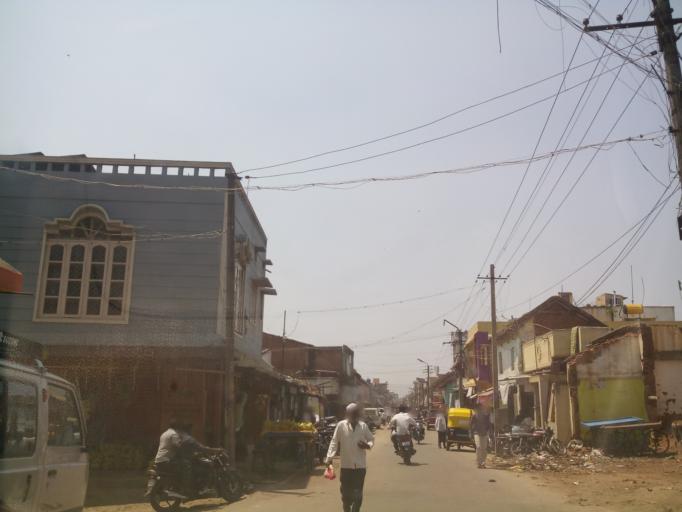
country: IN
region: Karnataka
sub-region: Hassan
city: Hassan
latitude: 13.0056
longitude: 76.0952
